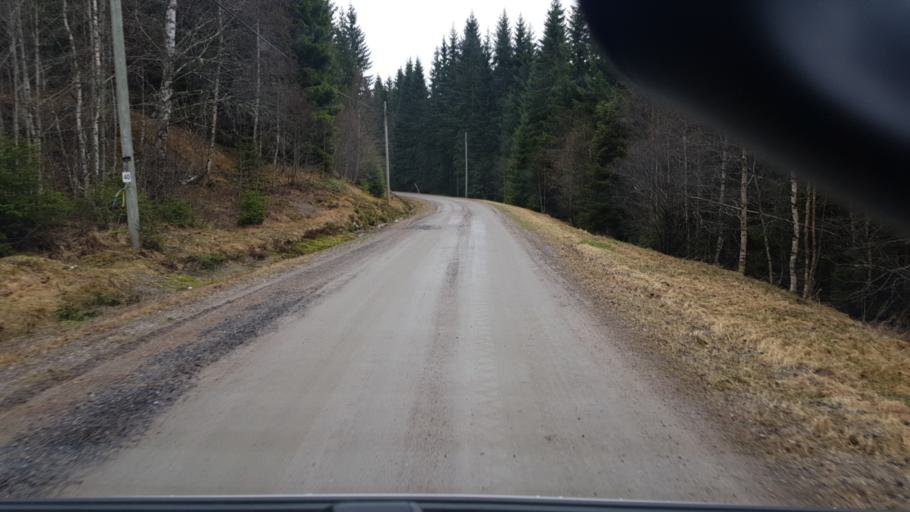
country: SE
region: Vaermland
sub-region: Eda Kommun
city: Charlottenberg
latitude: 59.9287
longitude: 12.3742
